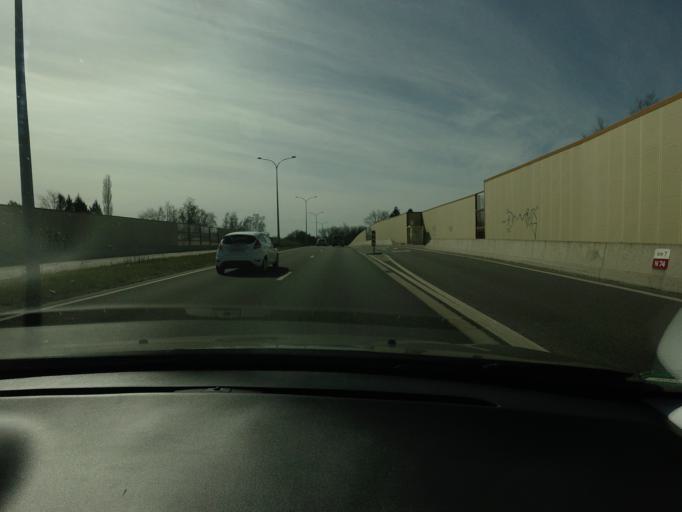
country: BE
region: Flanders
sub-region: Provincie Limburg
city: Zonhoven
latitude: 50.9938
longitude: 5.3609
